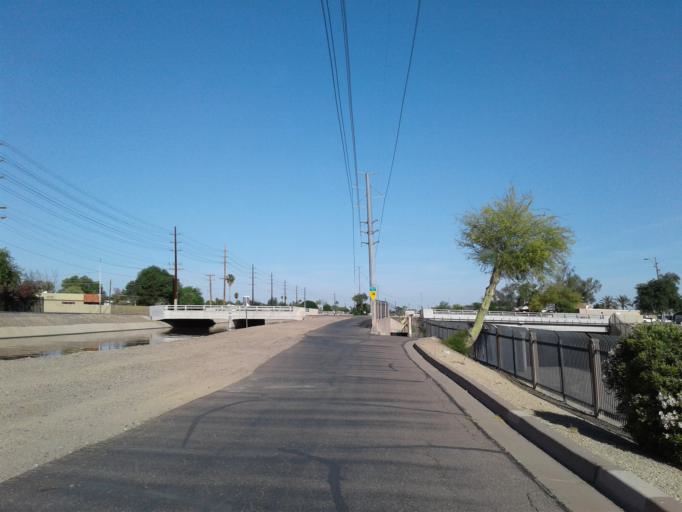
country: US
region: Arizona
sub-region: Maricopa County
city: Glendale
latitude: 33.5719
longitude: -112.1330
